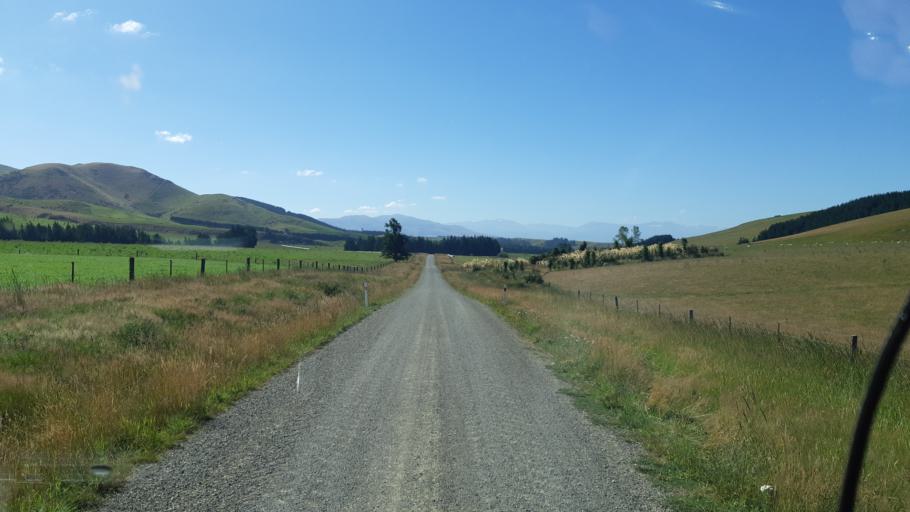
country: NZ
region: Canterbury
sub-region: Timaru District
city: Pleasant Point
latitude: -44.3260
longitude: 170.8622
